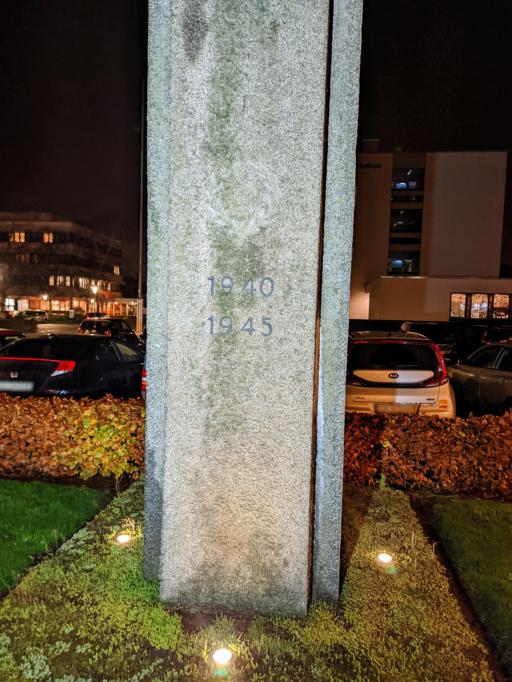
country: NO
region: Rogaland
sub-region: Time
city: Bryne
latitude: 58.7357
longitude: 5.6525
